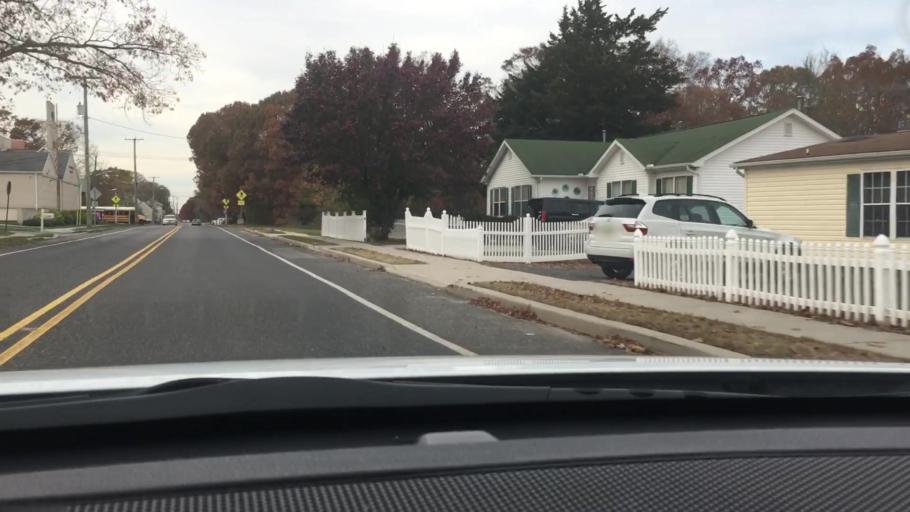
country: US
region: New Jersey
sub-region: Atlantic County
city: Northfield
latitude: 39.3860
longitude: -74.5462
